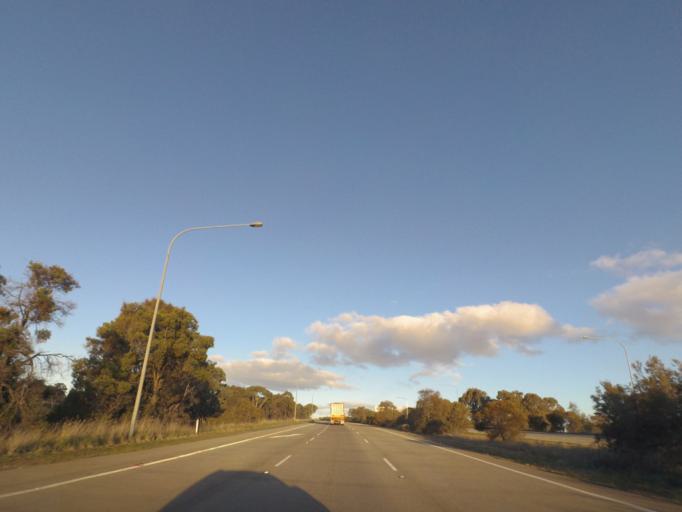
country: AU
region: New South Wales
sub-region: Yass Valley
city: Yass
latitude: -34.8040
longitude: 148.8799
